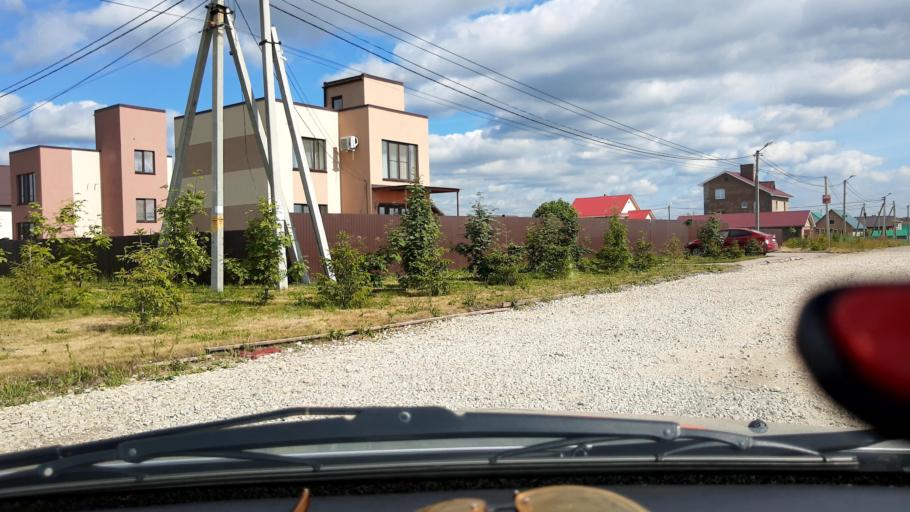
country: RU
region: Bashkortostan
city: Kabakovo
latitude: 54.6192
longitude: 56.0862
